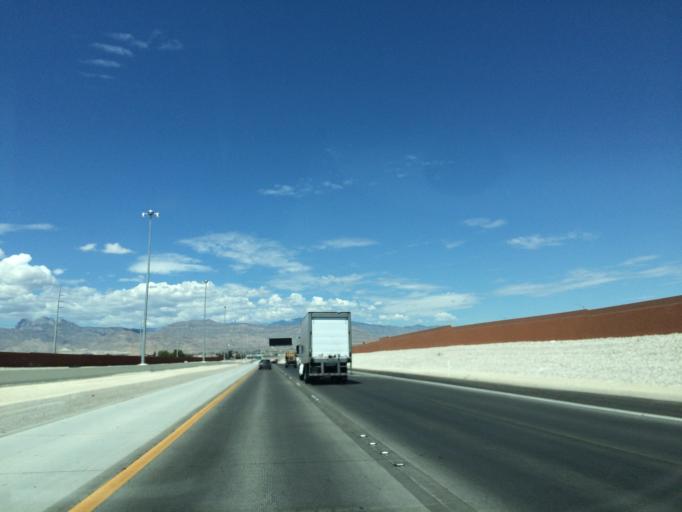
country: US
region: Nevada
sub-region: Clark County
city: North Las Vegas
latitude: 36.2755
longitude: -115.2320
